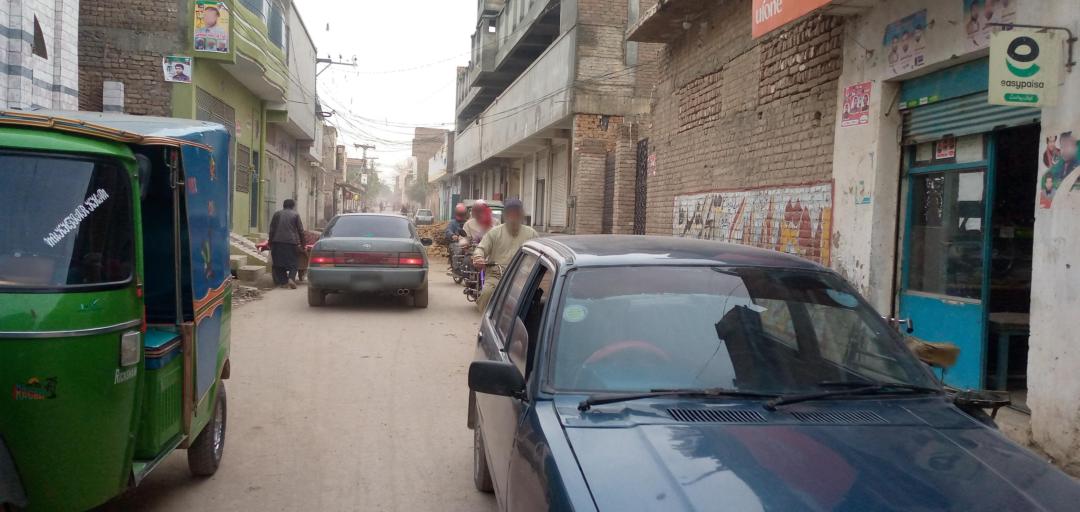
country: PK
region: Khyber Pakhtunkhwa
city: Peshawar
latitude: 34.0164
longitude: 71.5000
